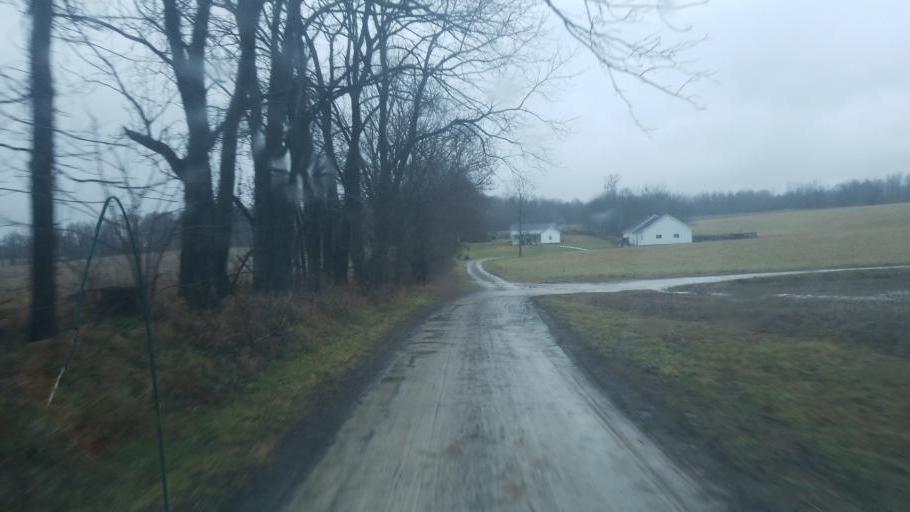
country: US
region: Ohio
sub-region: Morrow County
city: Mount Gilead
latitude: 40.5584
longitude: -82.6809
